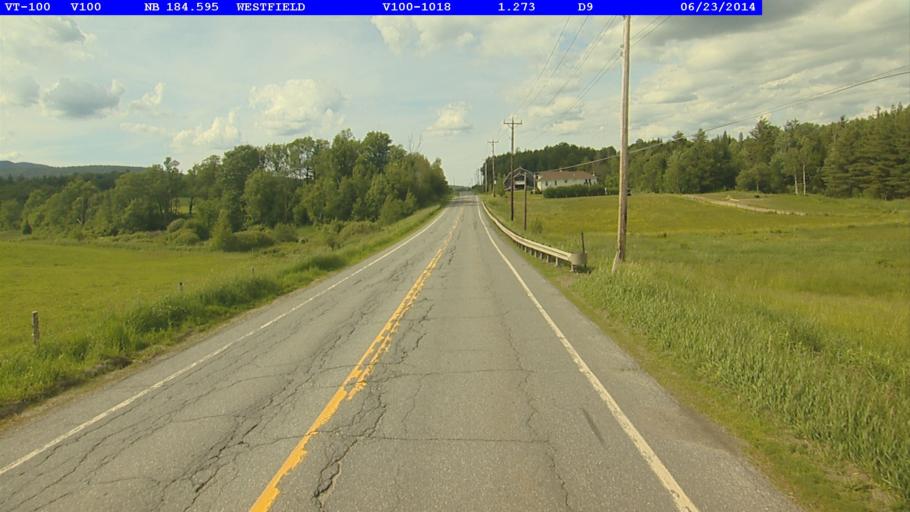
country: US
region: Vermont
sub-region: Orleans County
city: Newport
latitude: 44.8533
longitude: -72.4341
